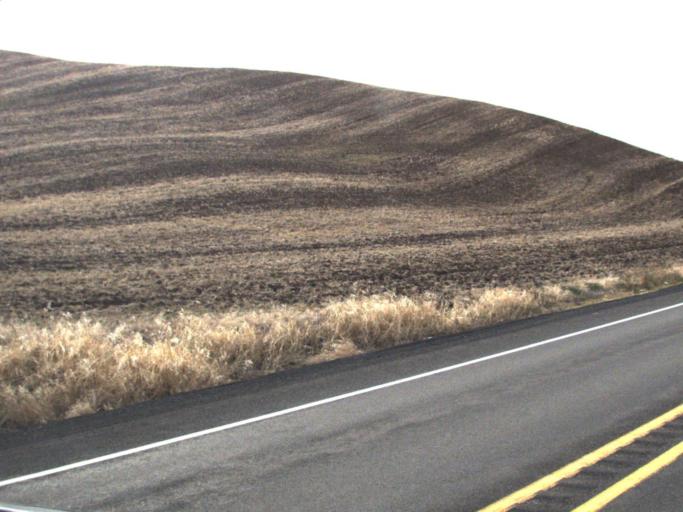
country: US
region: Washington
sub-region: Whitman County
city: Colfax
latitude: 46.8637
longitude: -117.4432
